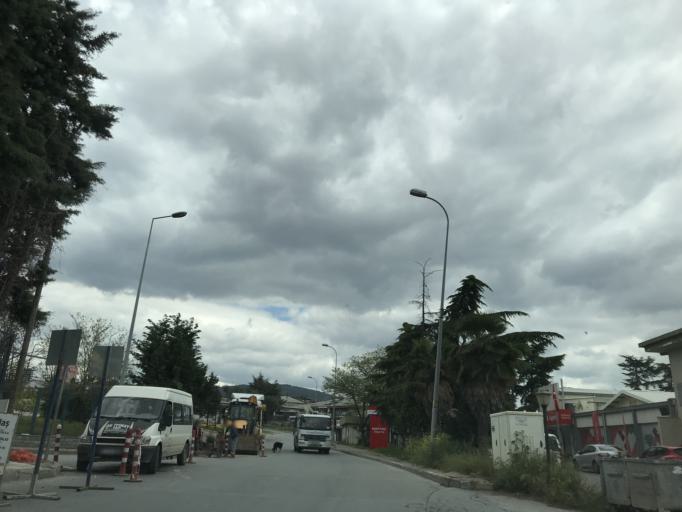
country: TR
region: Istanbul
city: Maltepe
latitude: 40.9000
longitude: 29.2049
